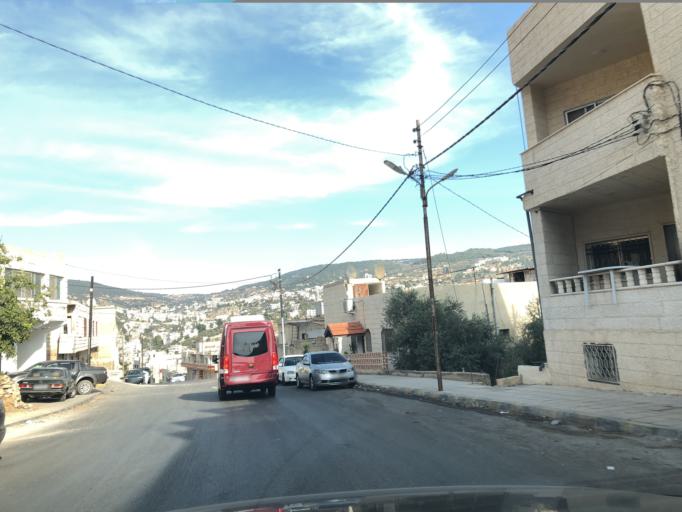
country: JO
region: Ajlun
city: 'Ajlun
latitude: 32.3309
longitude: 35.7442
